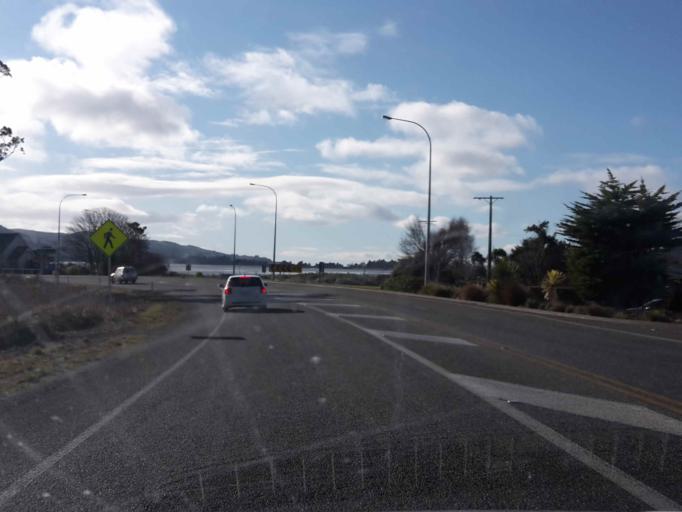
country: NZ
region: Otago
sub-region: Dunedin City
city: Portobello
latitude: -45.7476
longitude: 170.5682
